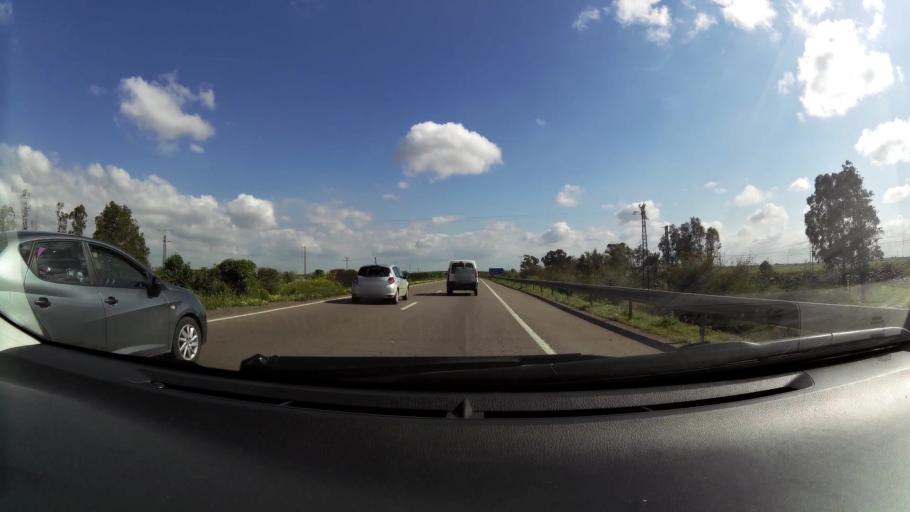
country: MA
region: Chaouia-Ouardigha
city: Nouaseur
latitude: 33.3634
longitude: -7.6197
